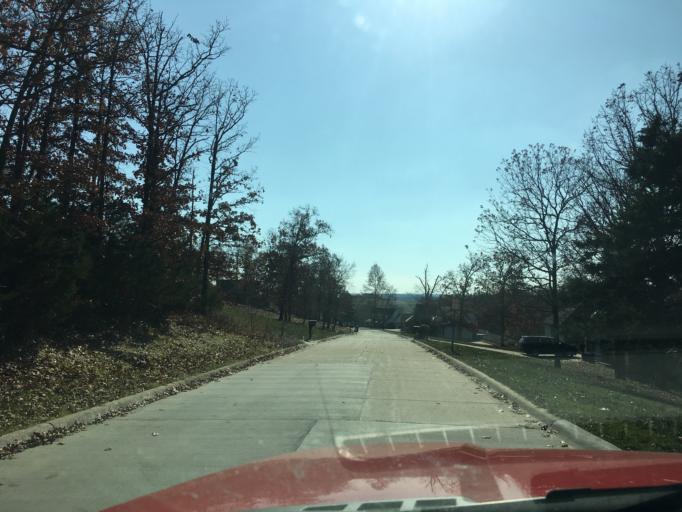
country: US
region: Missouri
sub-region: Cole County
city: Wardsville
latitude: 38.4827
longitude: -92.1794
